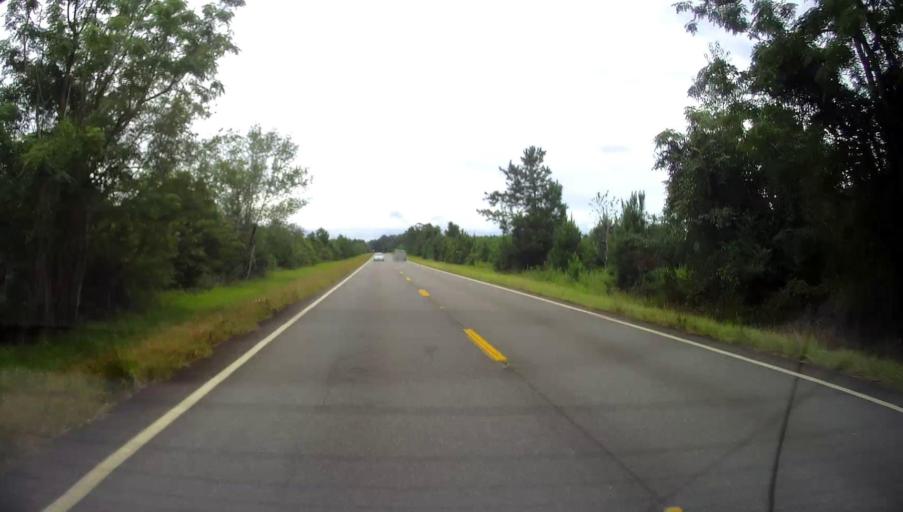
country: US
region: Georgia
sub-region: Marion County
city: Buena Vista
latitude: 32.2730
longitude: -84.4334
